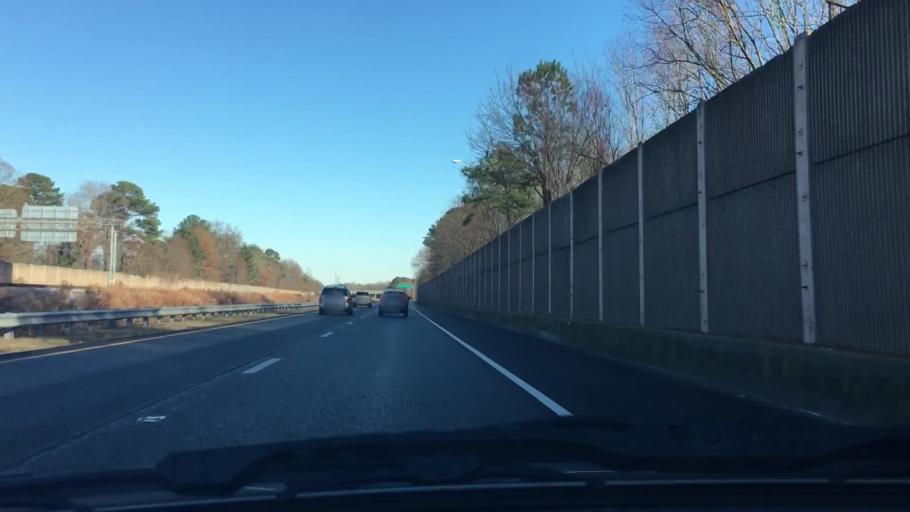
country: US
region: Virginia
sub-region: City of Portsmouth
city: Portsmouth Heights
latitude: 36.8687
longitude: -76.4100
